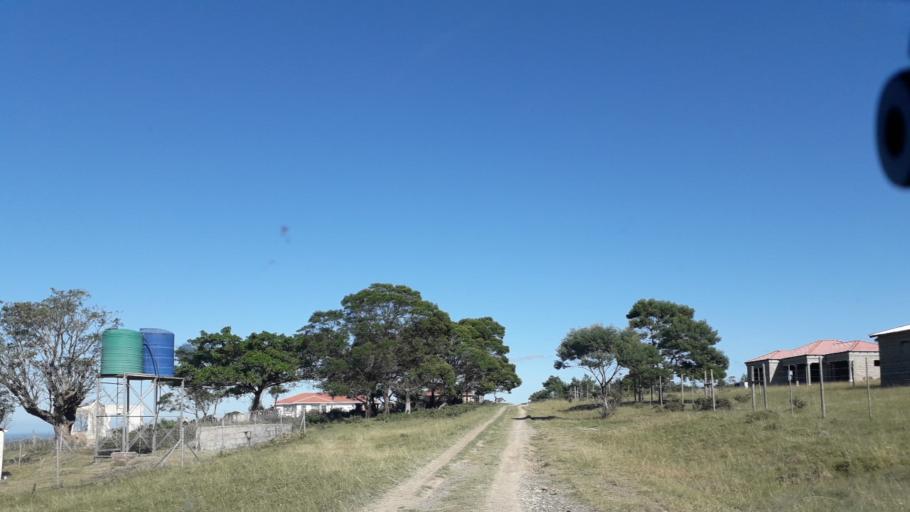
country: ZA
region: Eastern Cape
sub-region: Buffalo City Metropolitan Municipality
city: East London
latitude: -32.8228
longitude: 27.9626
